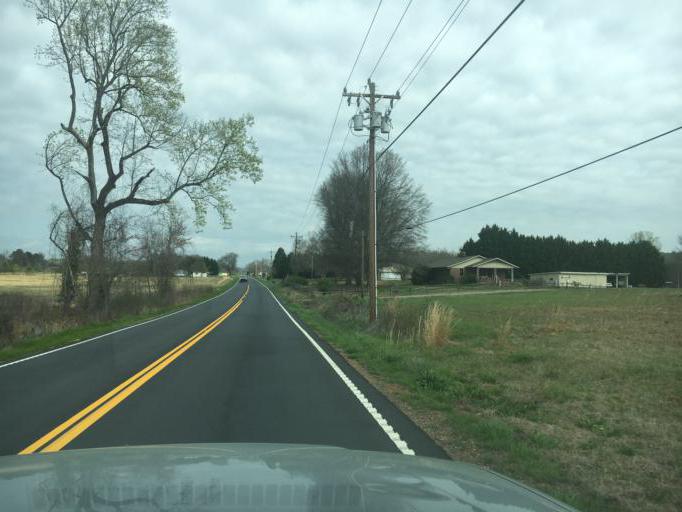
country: US
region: South Carolina
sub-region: Spartanburg County
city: Inman Mills
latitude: 35.0424
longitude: -82.1337
